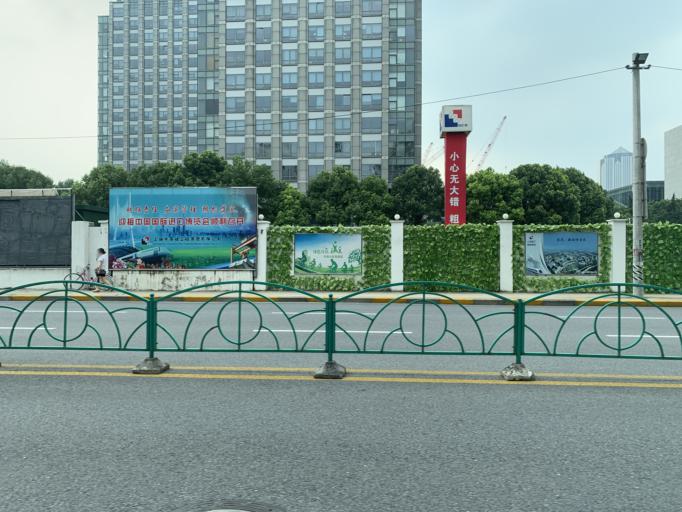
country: CN
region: Shanghai Shi
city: Huamu
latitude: 31.2231
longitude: 121.5474
